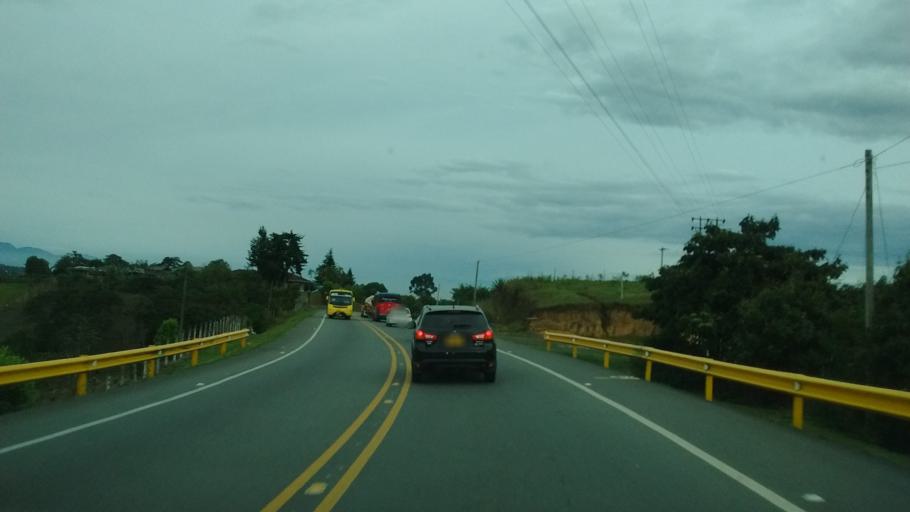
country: CO
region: Cauca
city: Morales
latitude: 2.7471
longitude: -76.5494
